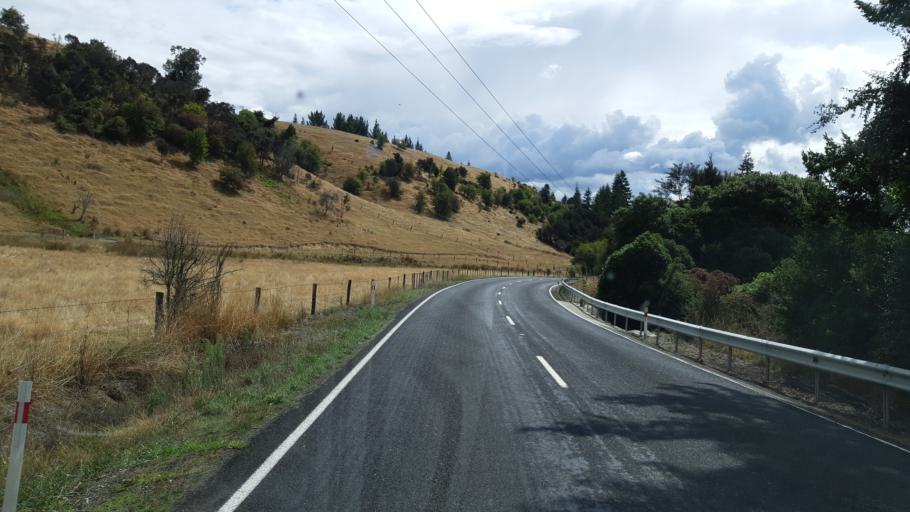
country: NZ
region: Tasman
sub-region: Tasman District
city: Wakefield
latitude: -41.5048
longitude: 172.7950
